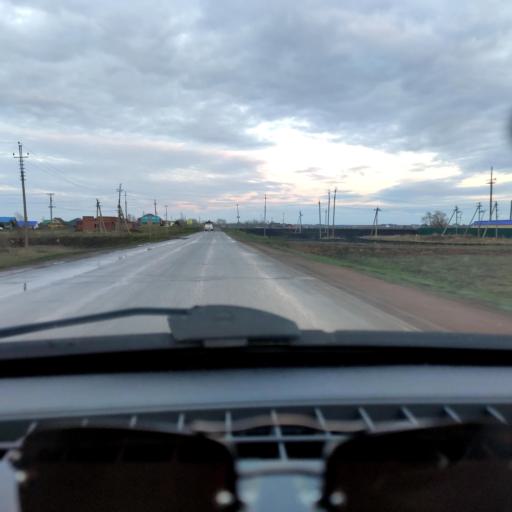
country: RU
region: Bashkortostan
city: Kabakovo
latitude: 54.5463
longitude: 56.1148
